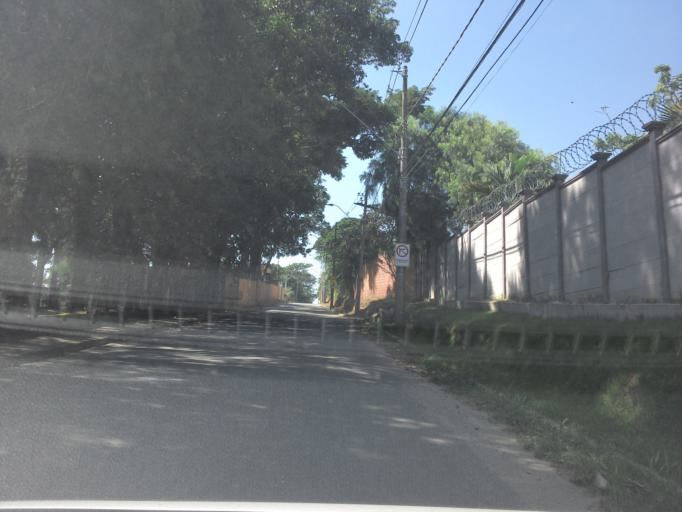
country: BR
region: Sao Paulo
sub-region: Vinhedo
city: Vinhedo
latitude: -23.0105
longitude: -47.0113
